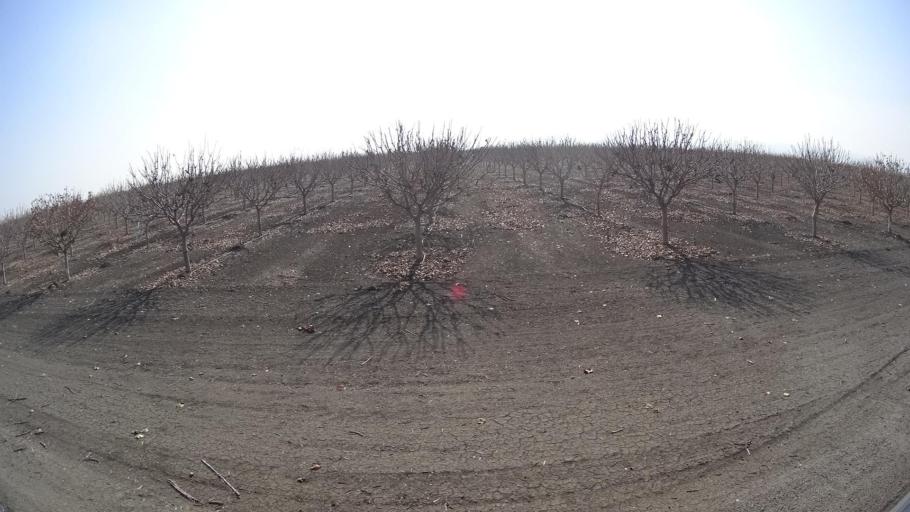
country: US
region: California
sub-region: Kern County
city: Buttonwillow
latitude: 35.3402
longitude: -119.4154
